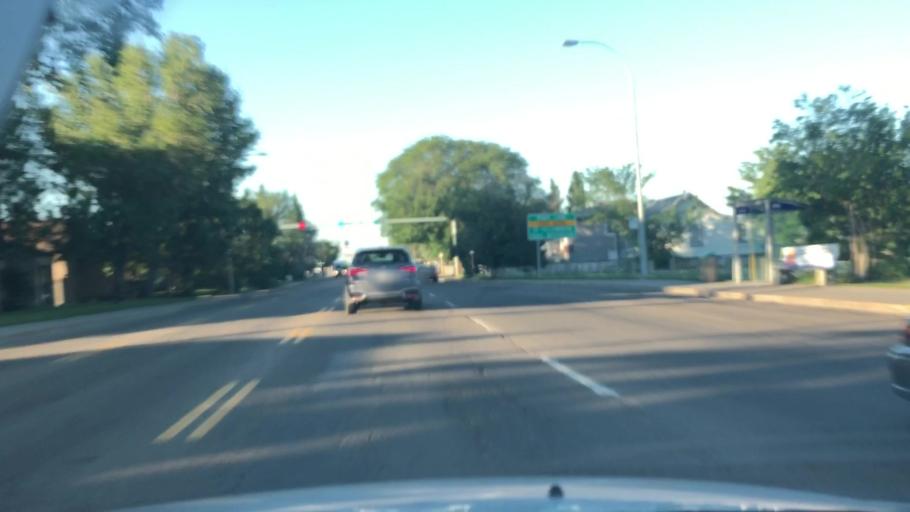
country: CA
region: Alberta
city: Edmonton
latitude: 53.5874
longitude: -113.5412
